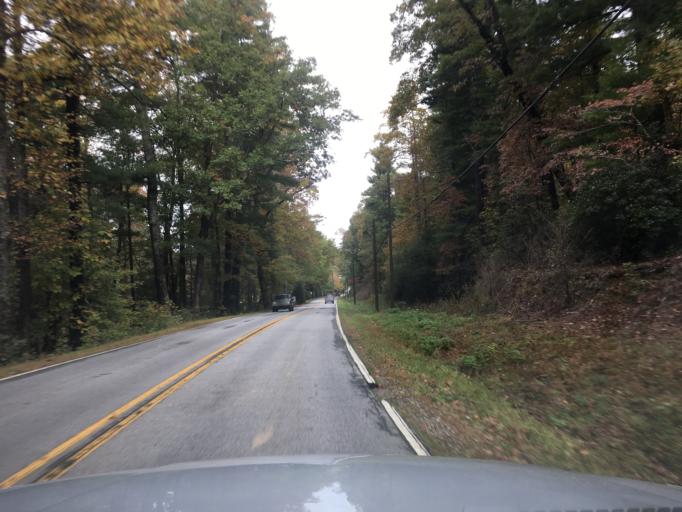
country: US
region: North Carolina
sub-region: Henderson County
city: Flat Rock
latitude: 35.2522
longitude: -82.4347
